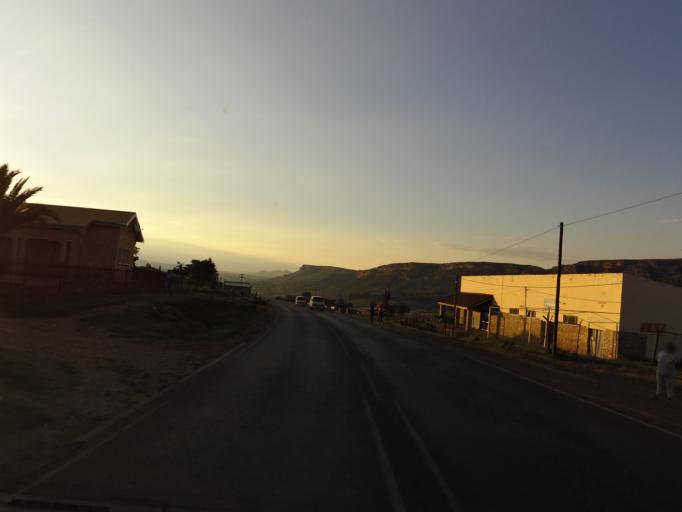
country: LS
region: Leribe
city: Leribe
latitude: -28.8841
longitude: 28.1052
